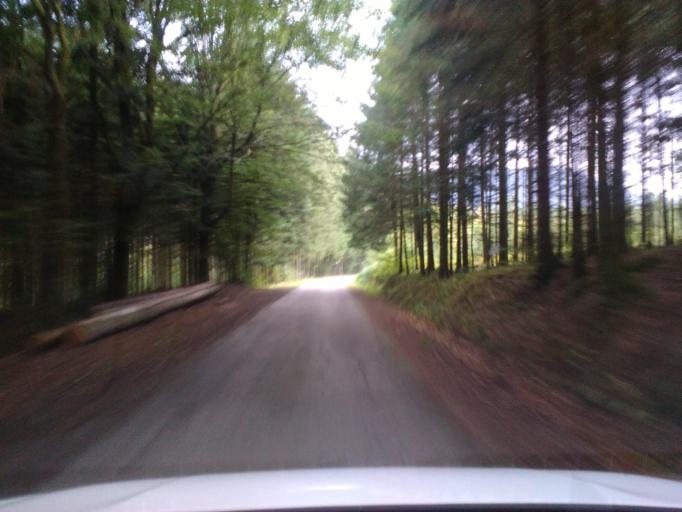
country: FR
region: Lorraine
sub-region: Departement des Vosges
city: Senones
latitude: 48.4060
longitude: 7.0358
